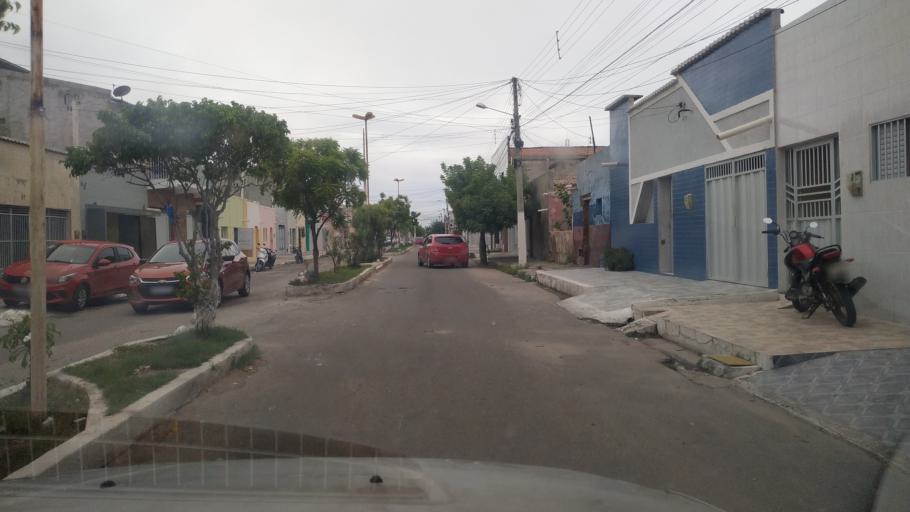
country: BR
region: Rio Grande do Norte
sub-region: Areia Branca
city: Areia Branca
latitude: -4.9573
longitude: -37.1321
